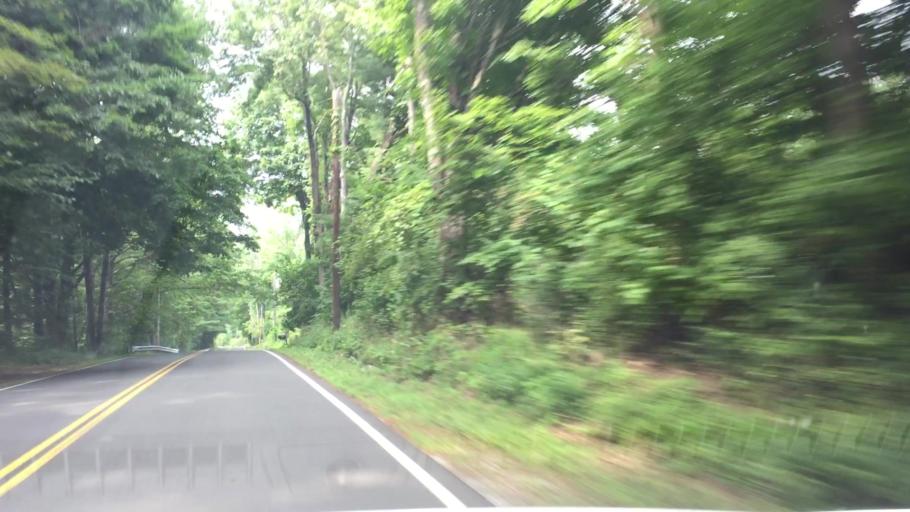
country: US
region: Massachusetts
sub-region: Berkshire County
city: Housatonic
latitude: 42.2225
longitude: -73.4052
